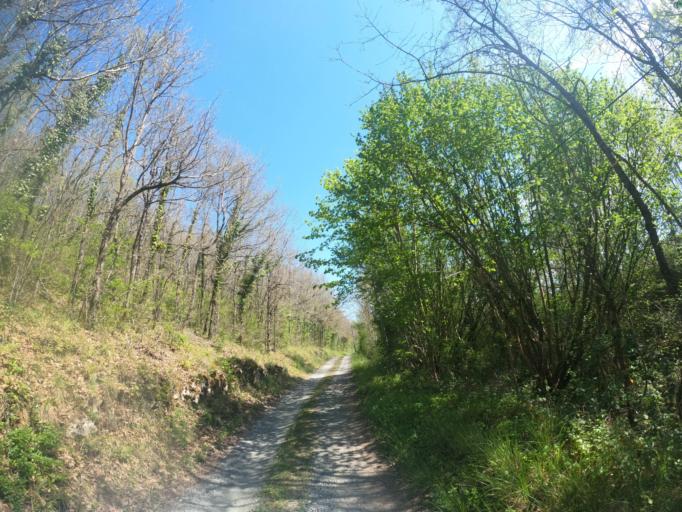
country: FR
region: Poitou-Charentes
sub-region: Departement des Deux-Sevres
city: Airvault
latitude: 46.8753
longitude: -0.1457
